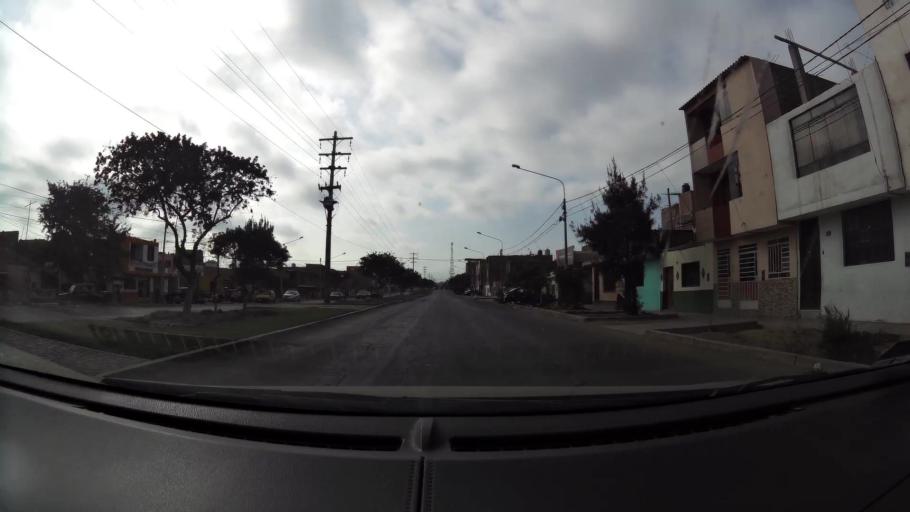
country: PE
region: La Libertad
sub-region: Provincia de Trujillo
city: La Esperanza
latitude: -8.0785
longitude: -79.0454
